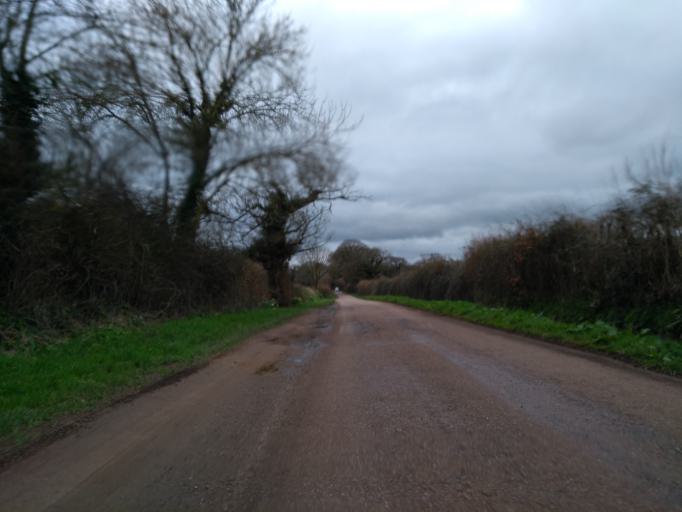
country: GB
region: England
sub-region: Devon
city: Bradninch
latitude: 50.8028
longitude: -3.4883
